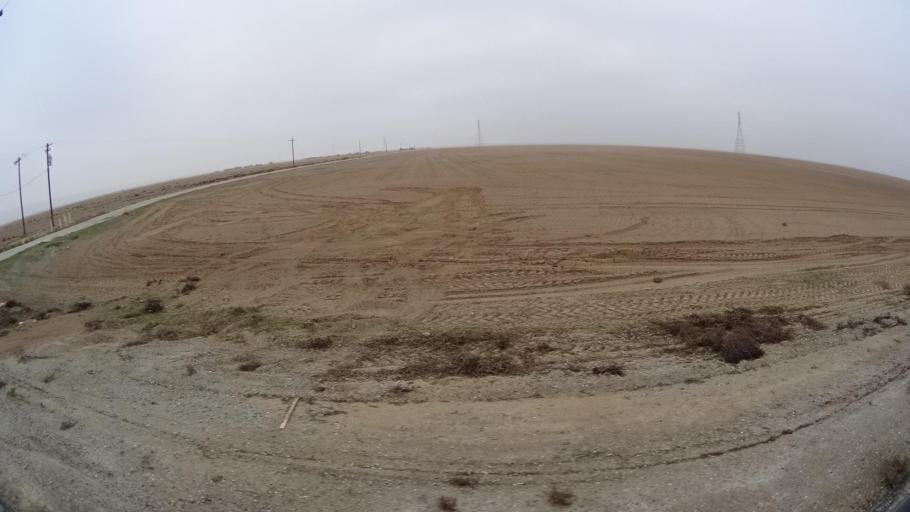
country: US
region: California
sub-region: Kern County
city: Maricopa
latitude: 35.1229
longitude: -119.3046
